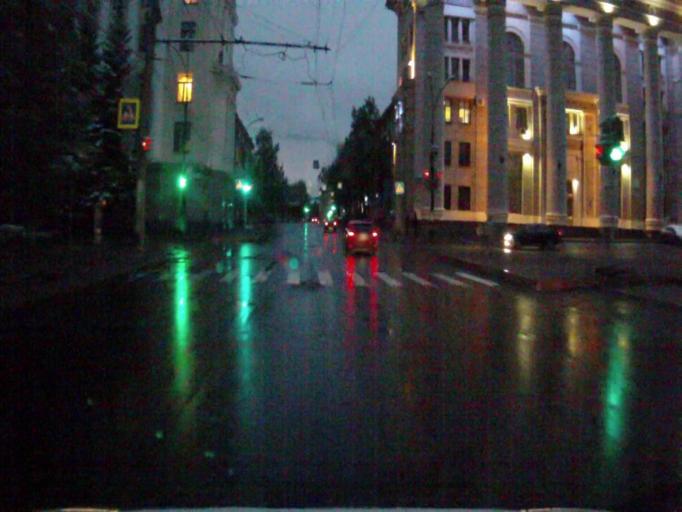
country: RU
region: Chelyabinsk
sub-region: Gorod Chelyabinsk
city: Chelyabinsk
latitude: 55.1576
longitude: 61.4031
